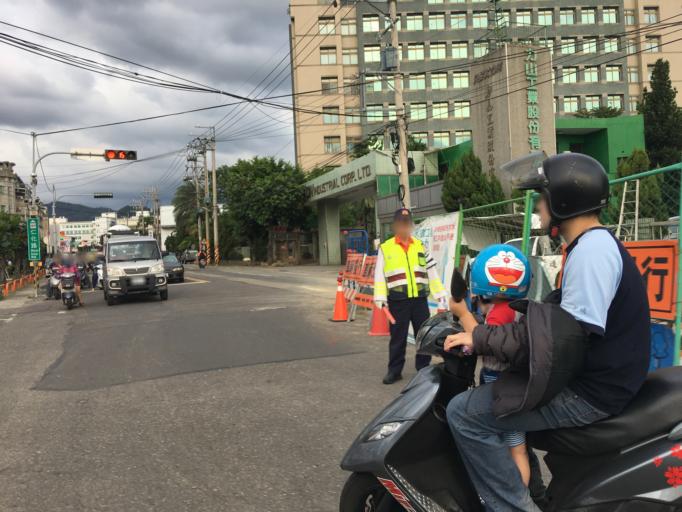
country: TW
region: Taiwan
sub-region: Taichung City
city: Taichung
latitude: 24.0942
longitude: 120.7137
